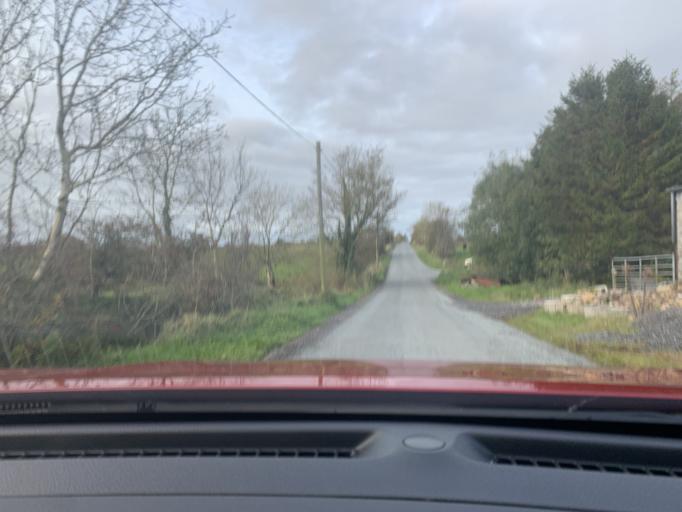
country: IE
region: Connaught
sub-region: Roscommon
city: Ballaghaderreen
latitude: 53.9851
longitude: -8.6148
